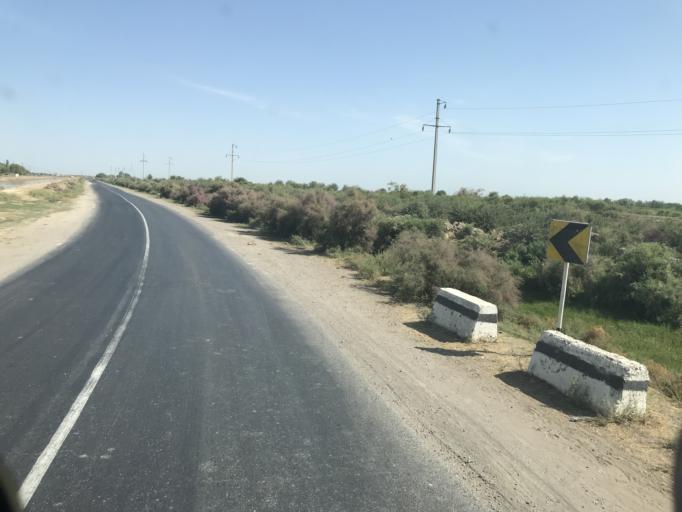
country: KZ
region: Ongtustik Qazaqstan
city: Myrzakent
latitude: 40.7166
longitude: 68.5344
